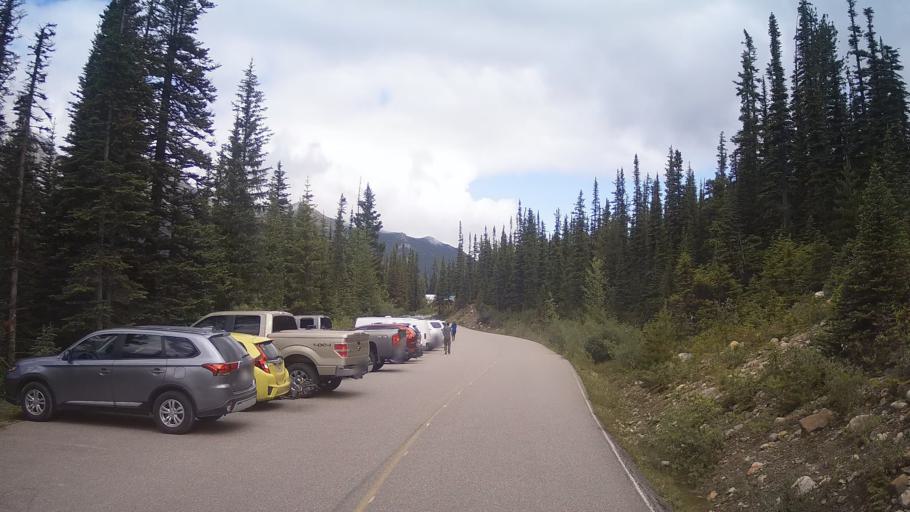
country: CA
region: Alberta
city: Jasper Park Lodge
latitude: 52.7015
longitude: -118.0598
